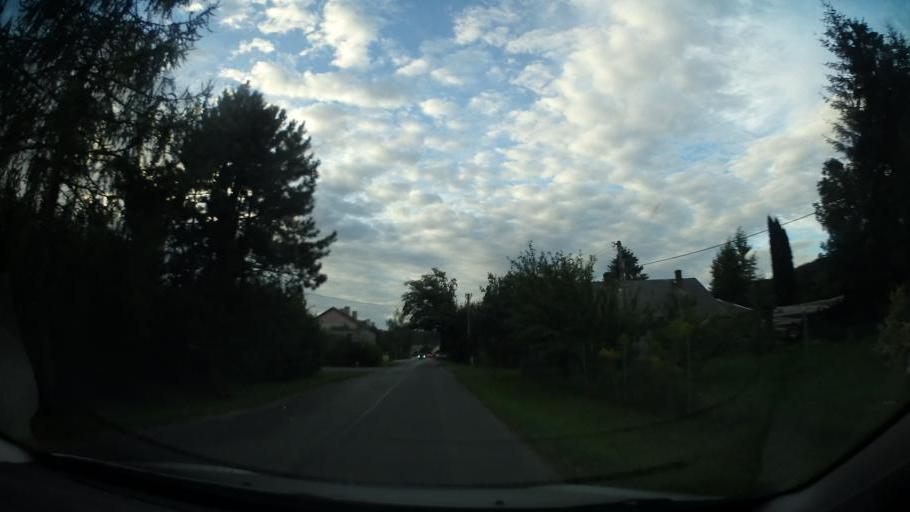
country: CZ
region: Olomoucky
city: Paseka
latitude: 49.8161
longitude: 17.2029
